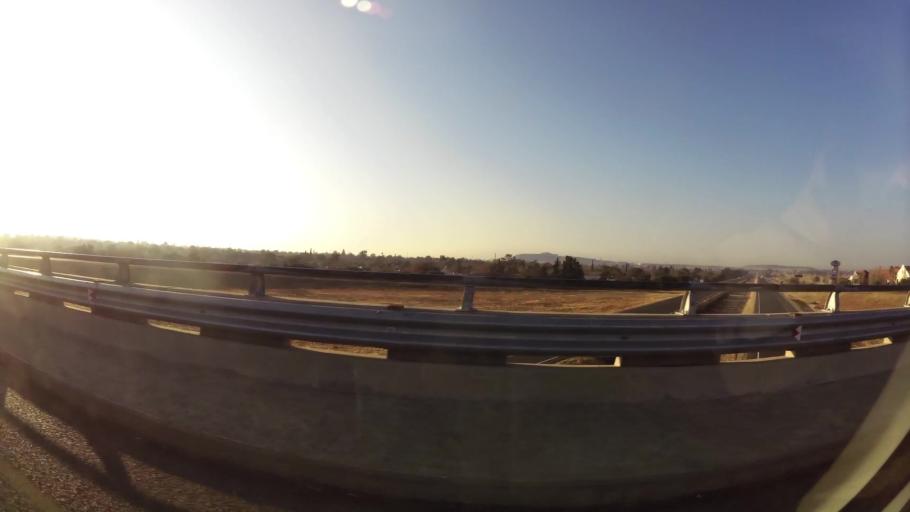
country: ZA
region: Orange Free State
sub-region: Mangaung Metropolitan Municipality
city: Bloemfontein
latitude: -29.1654
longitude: 26.1815
